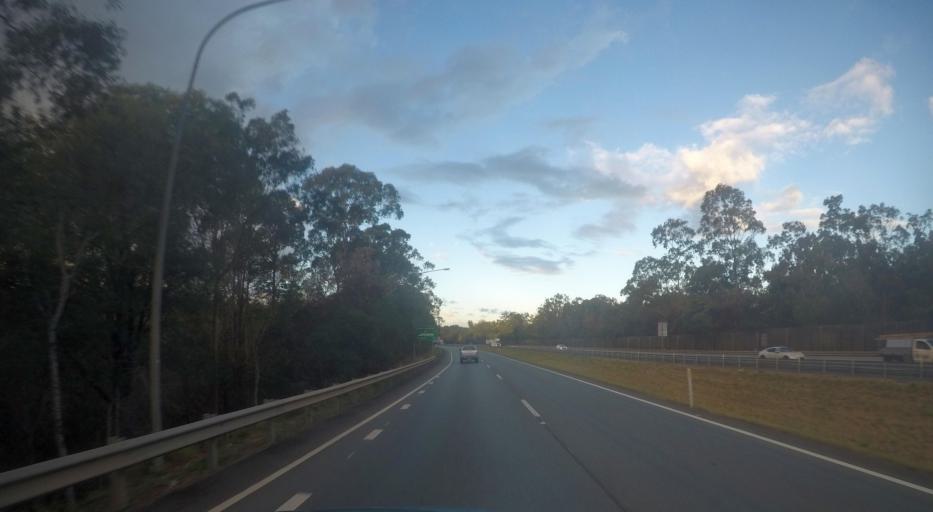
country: AU
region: Queensland
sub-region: Ipswich
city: Brassall
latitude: -27.5805
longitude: 152.7297
